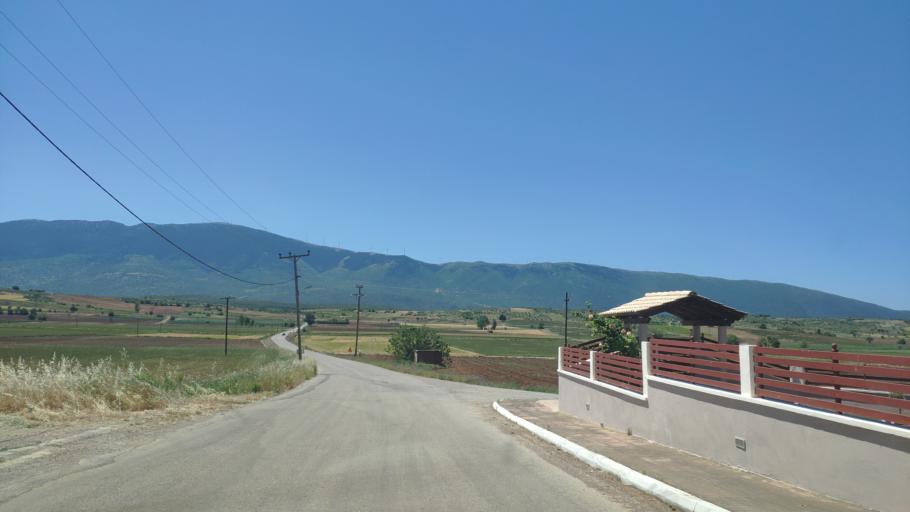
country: GR
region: Central Greece
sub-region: Nomos Voiotias
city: Kaparellion
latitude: 38.2632
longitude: 23.2349
